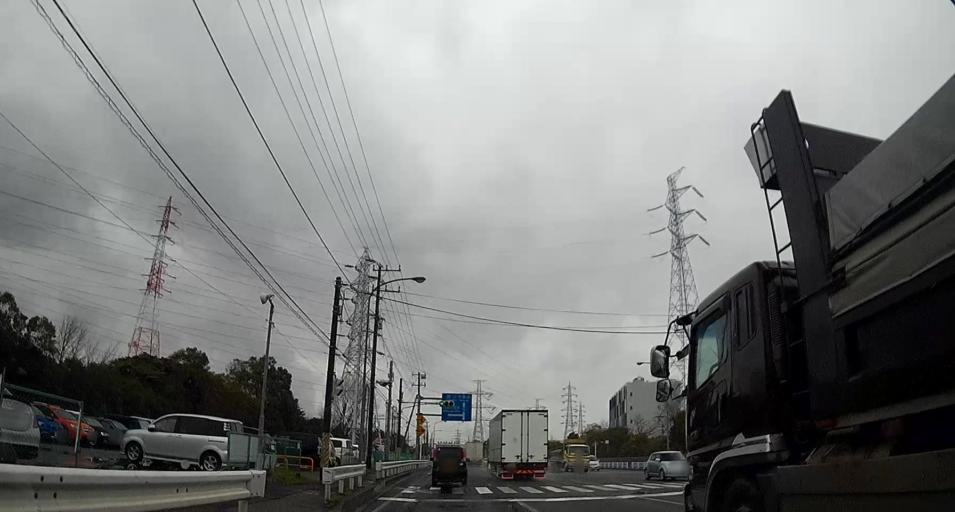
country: JP
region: Chiba
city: Ichihara
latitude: 35.5314
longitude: 140.0896
